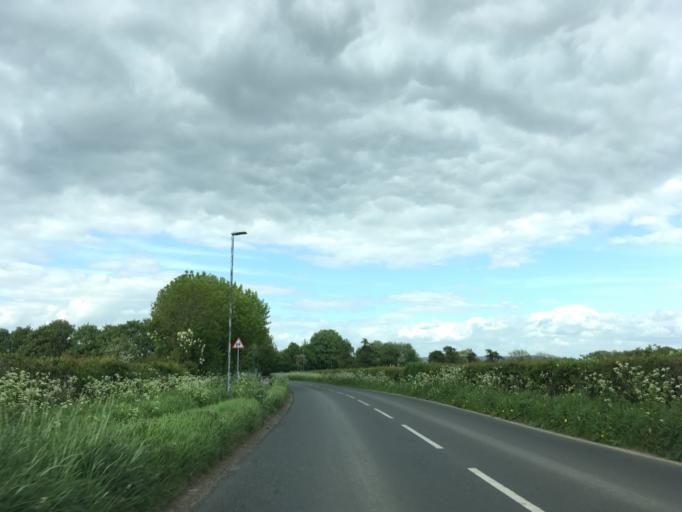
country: GB
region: England
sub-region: Gloucestershire
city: Dursley
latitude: 51.7155
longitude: -2.3608
